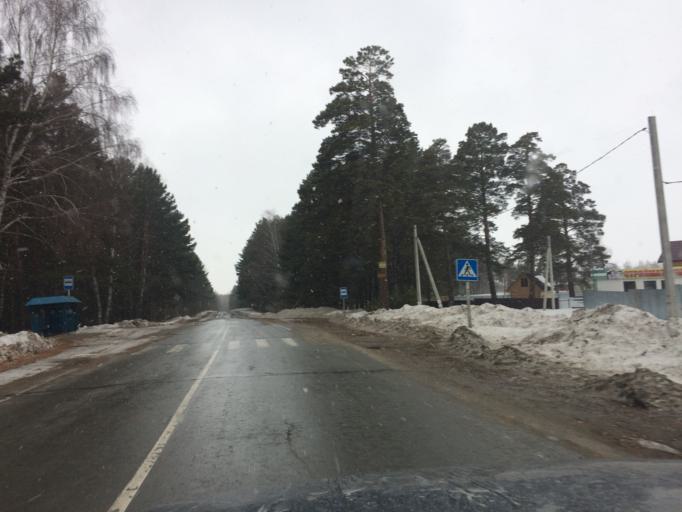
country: RU
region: Novosibirsk
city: Tashara
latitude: 55.4662
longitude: 83.2913
